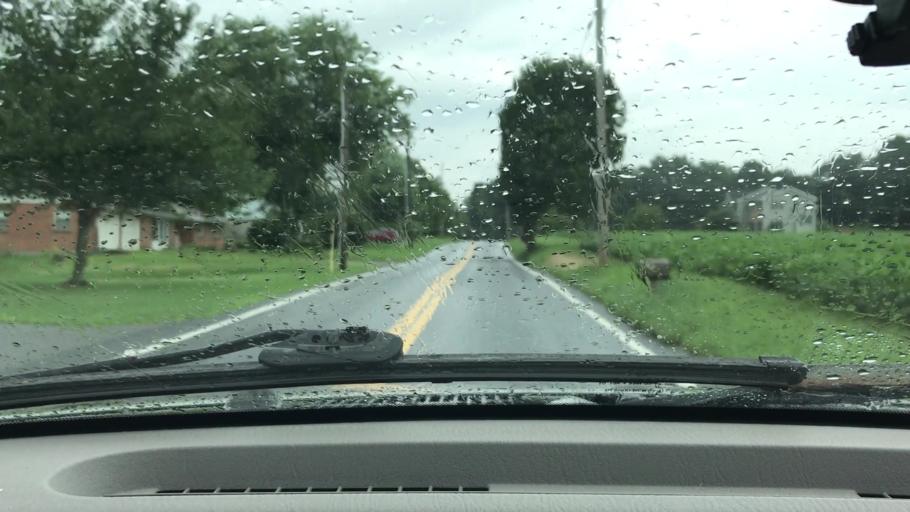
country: US
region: Pennsylvania
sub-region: Lancaster County
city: Elizabethtown
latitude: 40.2127
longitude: -76.6269
